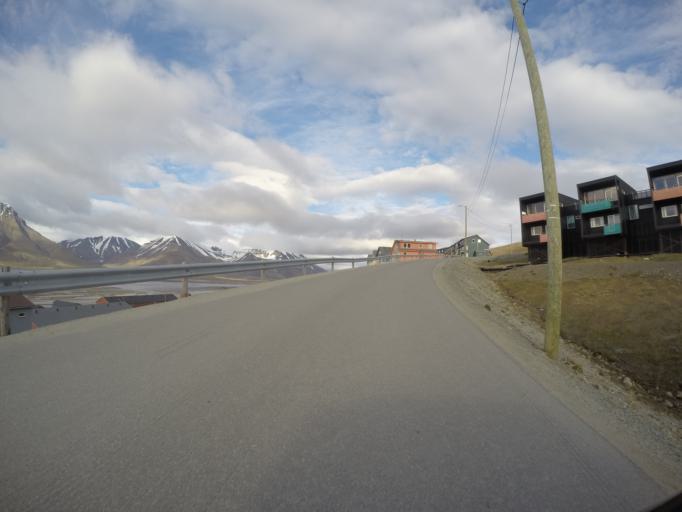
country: SJ
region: Svalbard
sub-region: Spitsbergen
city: Longyearbyen
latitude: 78.2183
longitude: 15.6616
